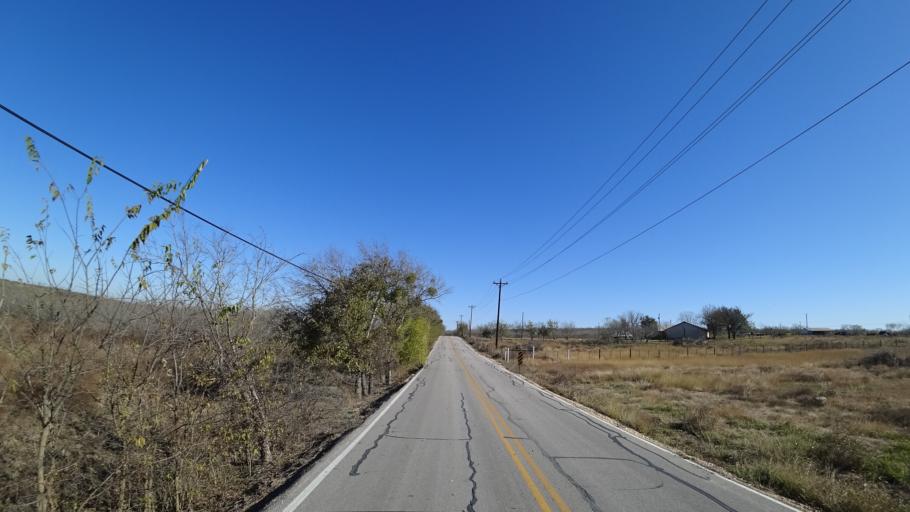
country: US
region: Texas
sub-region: Travis County
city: Onion Creek
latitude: 30.1094
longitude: -97.6716
